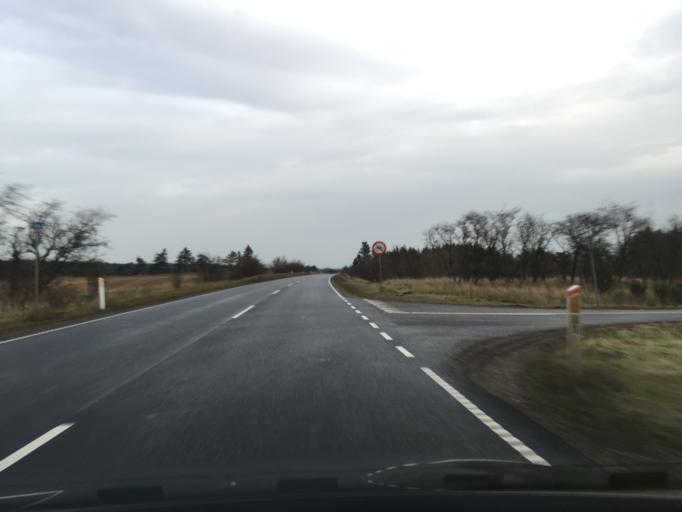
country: DK
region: Central Jutland
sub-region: Viborg Kommune
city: Bjerringbro
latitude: 56.3682
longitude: 9.6158
